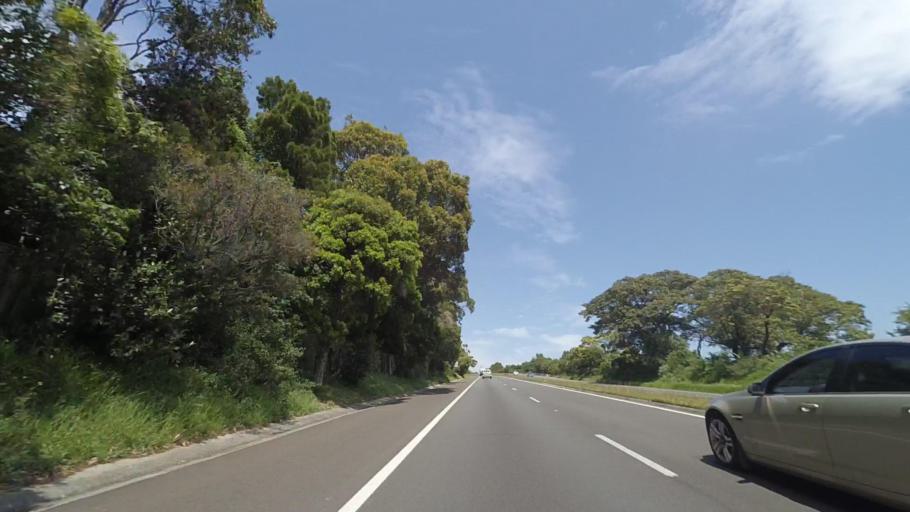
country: AU
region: New South Wales
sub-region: Kiama
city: Kiama
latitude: -34.6704
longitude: 150.8439
